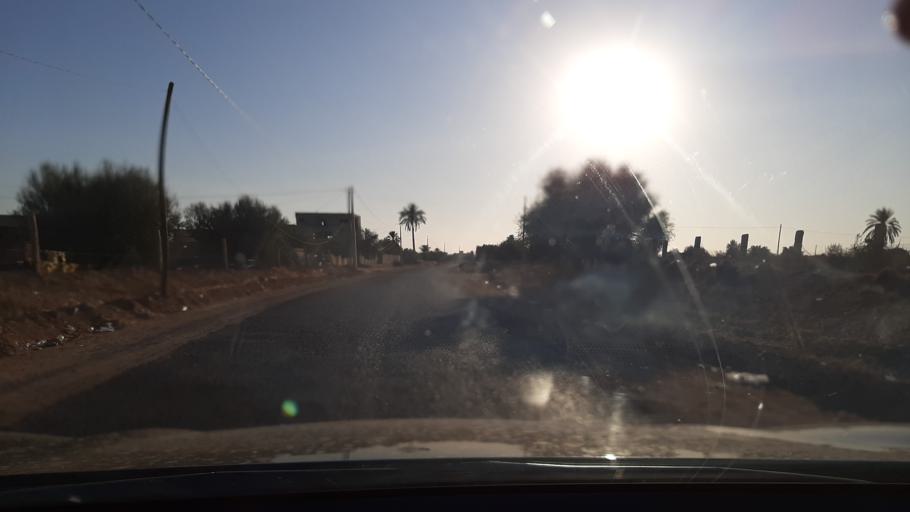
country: TN
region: Qabis
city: Matmata
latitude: 33.6177
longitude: 10.2642
